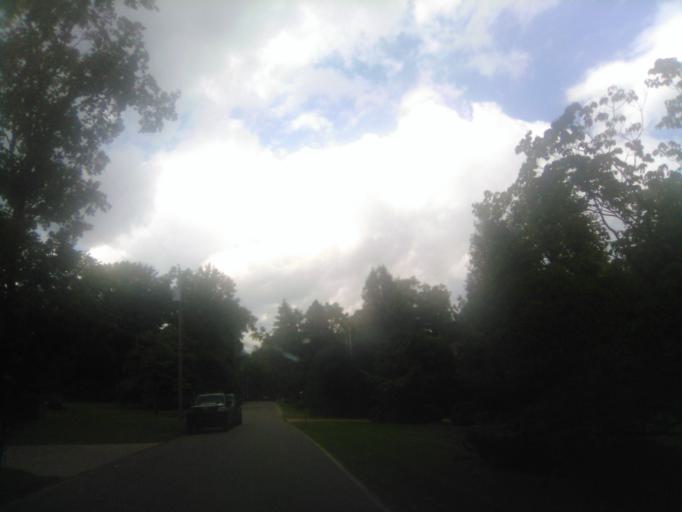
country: US
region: Tennessee
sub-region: Davidson County
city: Belle Meade
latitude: 36.1132
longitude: -86.8441
